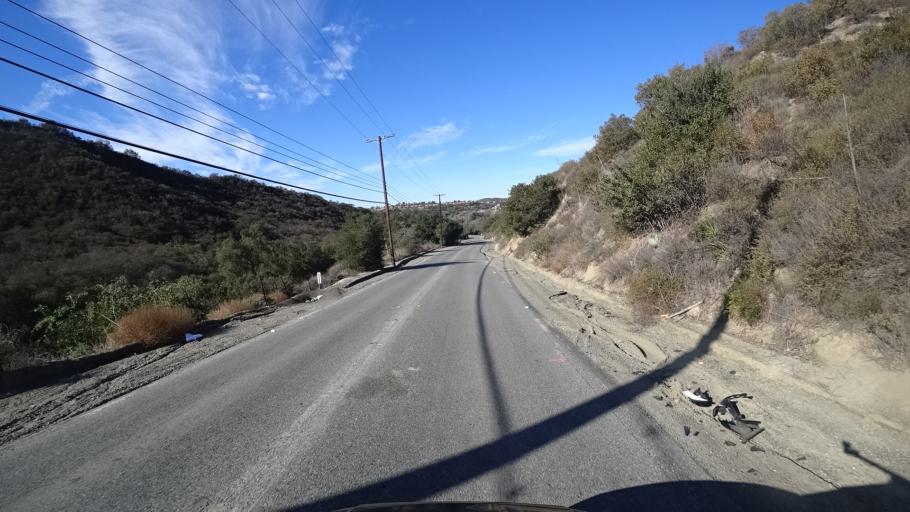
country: US
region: California
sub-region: Orange County
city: Portola Hills
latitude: 33.6861
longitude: -117.6082
